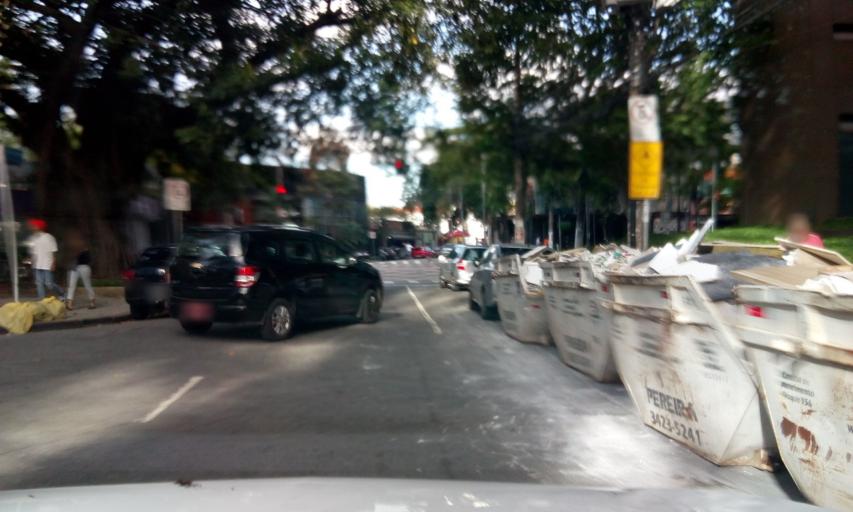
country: BR
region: Sao Paulo
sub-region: Sao Paulo
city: Sao Paulo
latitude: -23.6025
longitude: -46.6925
